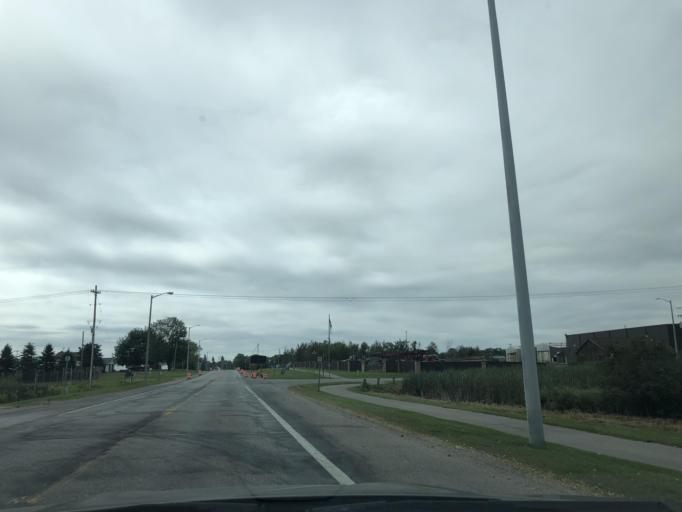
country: US
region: Michigan
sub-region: Missaukee County
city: Lake City
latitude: 44.2005
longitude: -85.2140
